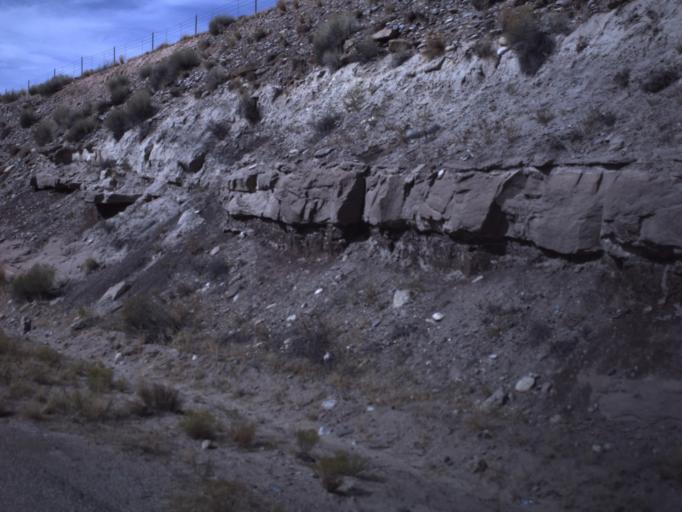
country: US
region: Utah
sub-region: San Juan County
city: Blanding
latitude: 37.2686
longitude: -109.3019
